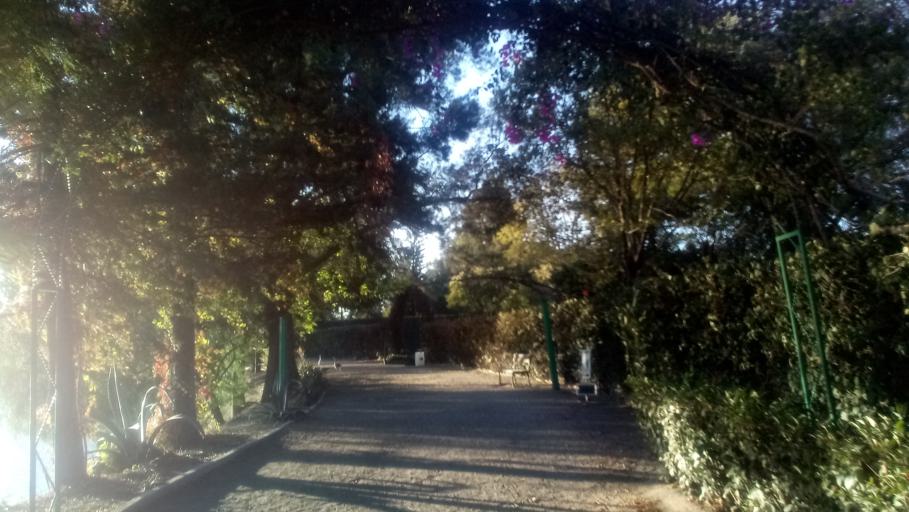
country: MX
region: Puebla
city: Puebla
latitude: 19.0078
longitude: -98.2126
